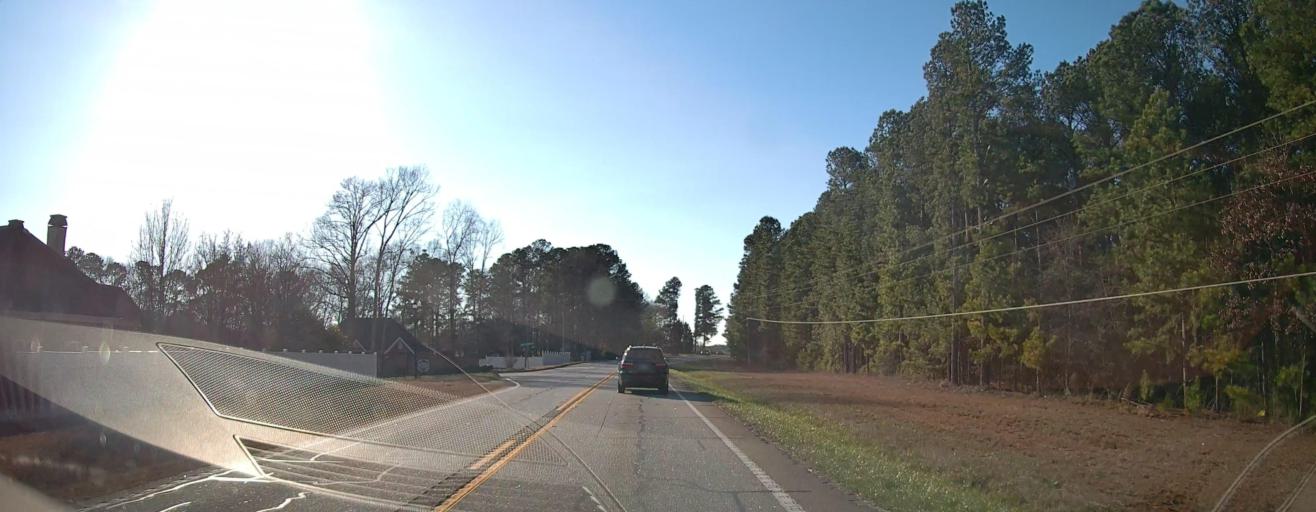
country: US
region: Georgia
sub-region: Henry County
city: Hampton
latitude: 33.4191
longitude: -84.2591
